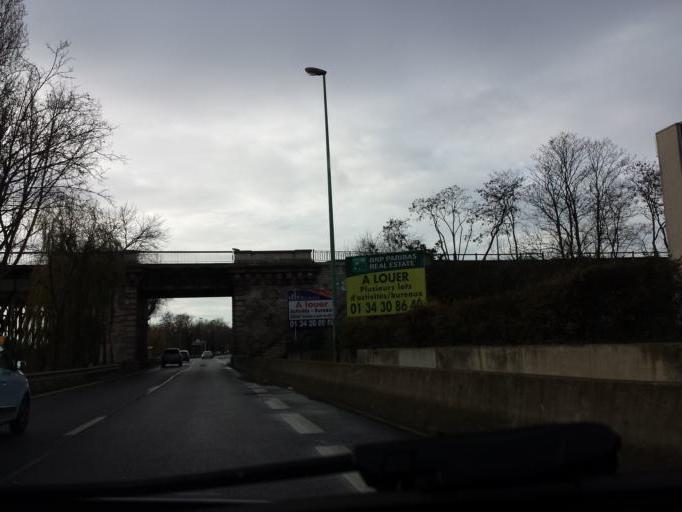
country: FR
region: Ile-de-France
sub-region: Departement du Val-d'Oise
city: Argenteuil
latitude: 48.9340
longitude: 2.2412
